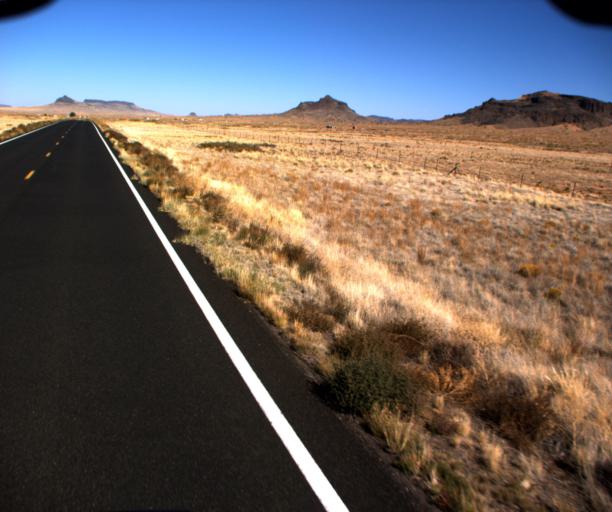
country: US
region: Arizona
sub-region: Navajo County
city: Dilkon
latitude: 35.4564
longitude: -110.4229
